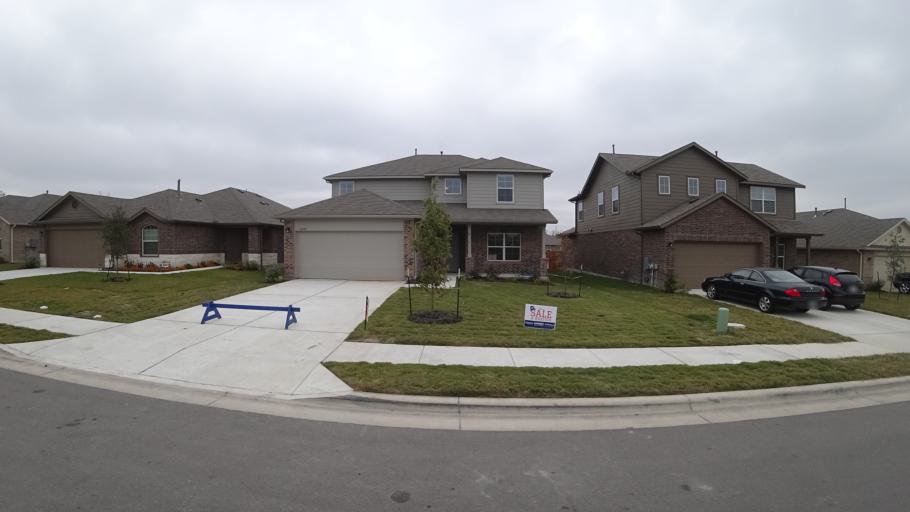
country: US
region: Texas
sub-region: Travis County
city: Pflugerville
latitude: 30.3694
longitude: -97.6492
